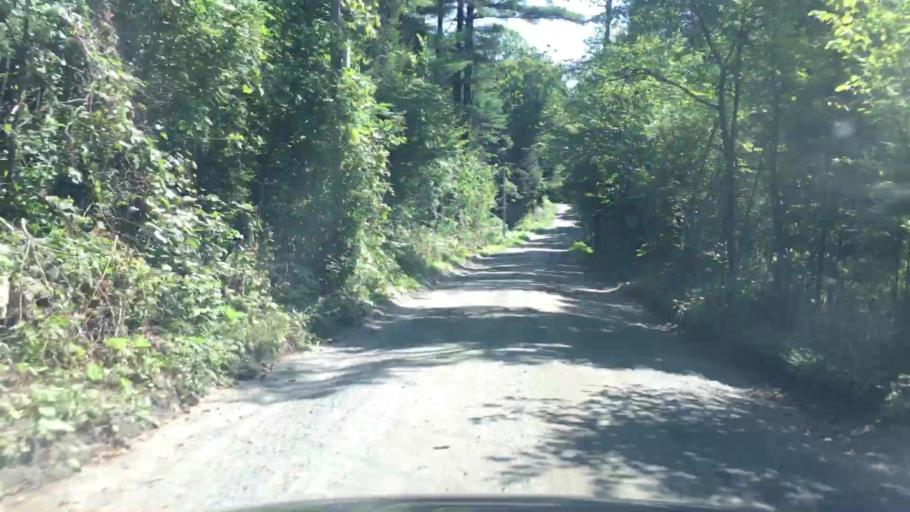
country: US
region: Vermont
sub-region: Windham County
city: West Brattleboro
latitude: 42.7987
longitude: -72.6397
